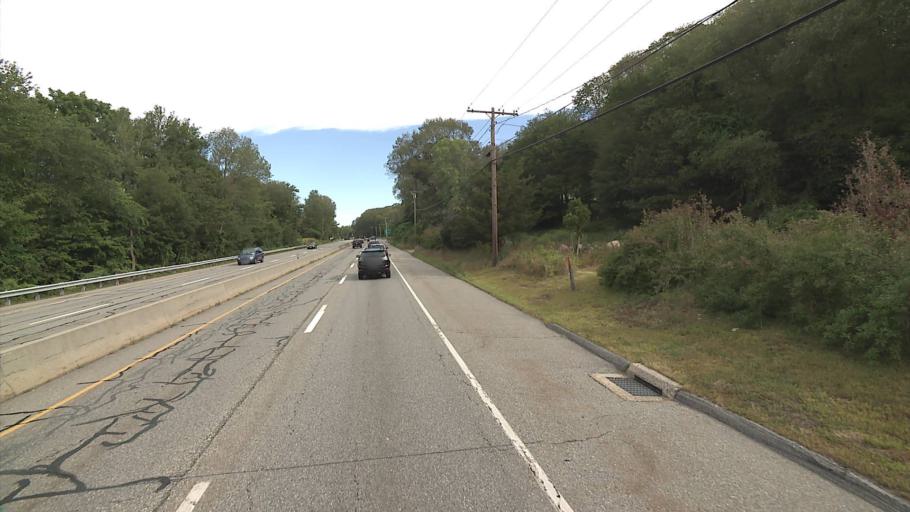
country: US
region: Connecticut
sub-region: New London County
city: Uncasville
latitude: 41.4059
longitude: -72.1061
